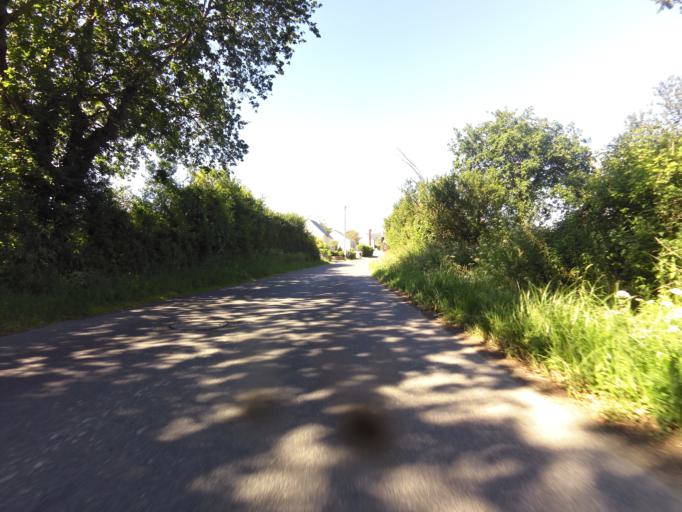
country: FR
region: Brittany
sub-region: Departement du Morbihan
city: Penestin
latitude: 47.4643
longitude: -2.4825
